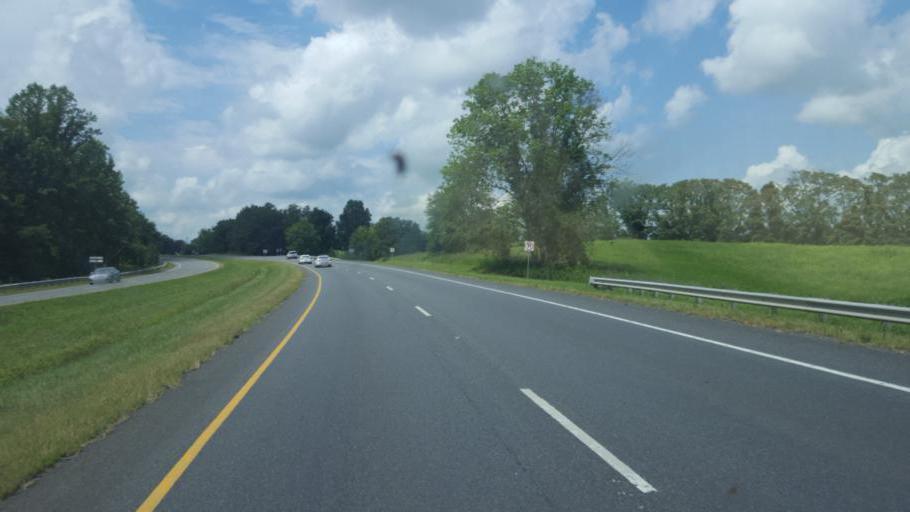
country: US
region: Virginia
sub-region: Fauquier County
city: Marshall
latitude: 38.8313
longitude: -77.8170
